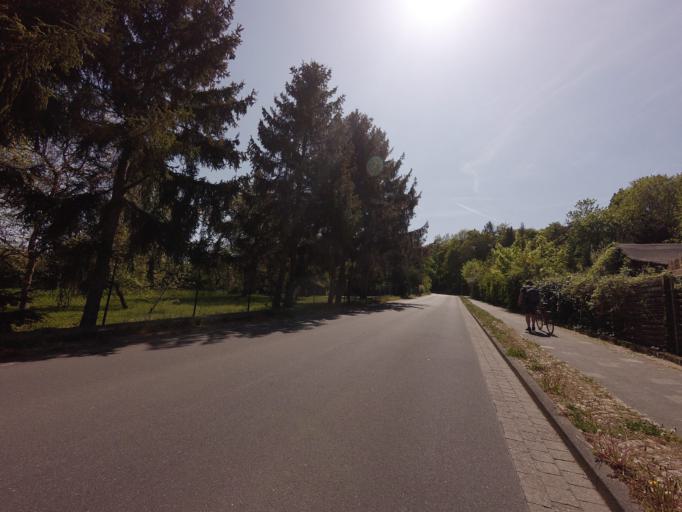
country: DE
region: Lower Saxony
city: Hildesheim
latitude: 52.1466
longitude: 9.9731
